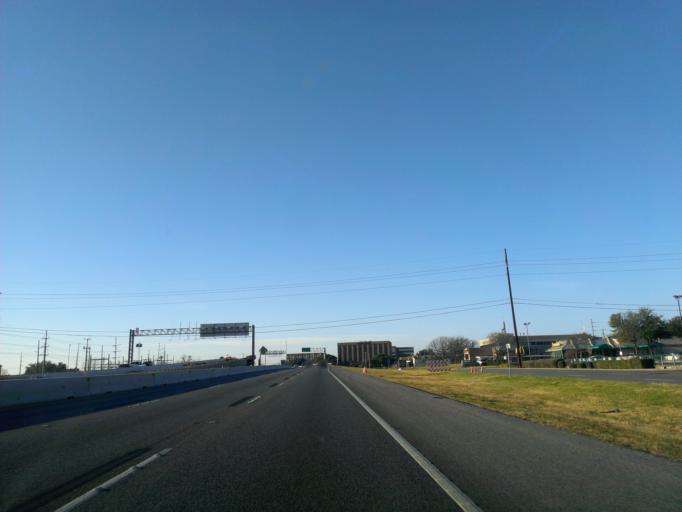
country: US
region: Texas
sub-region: Travis County
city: West Lake Hills
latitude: 30.3398
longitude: -97.7544
